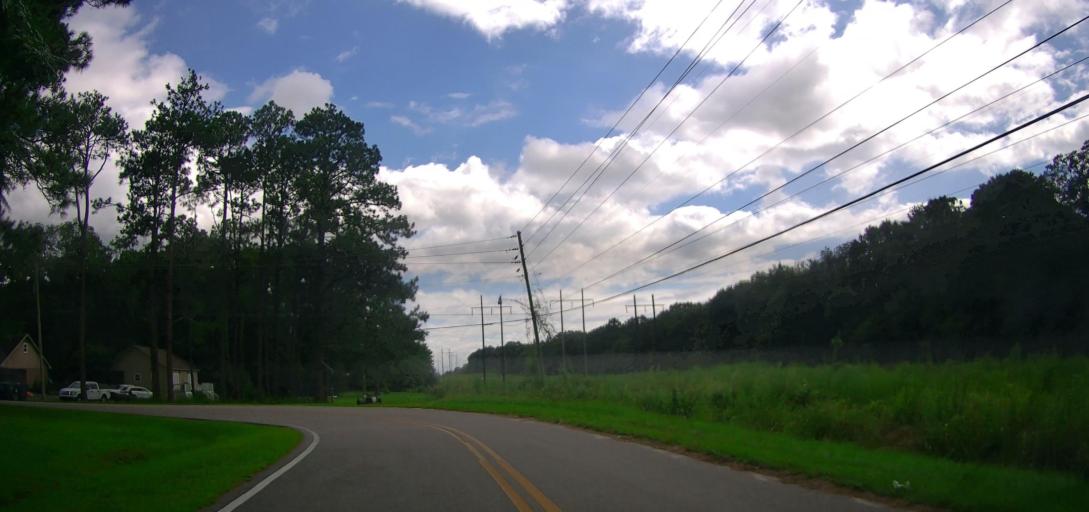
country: US
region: Georgia
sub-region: Ben Hill County
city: Fitzgerald
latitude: 31.7069
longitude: -83.2951
